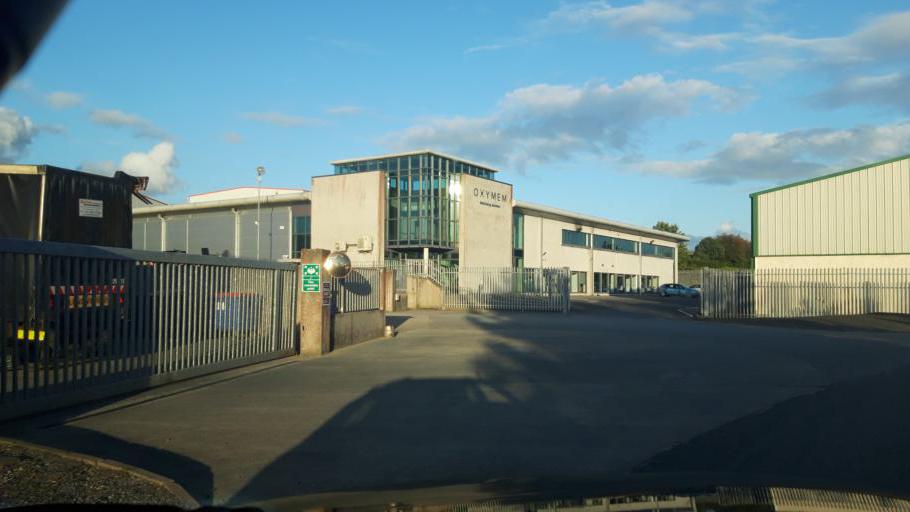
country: IE
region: Leinster
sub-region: An Iarmhi
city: Athlone
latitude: 53.4277
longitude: -7.8985
